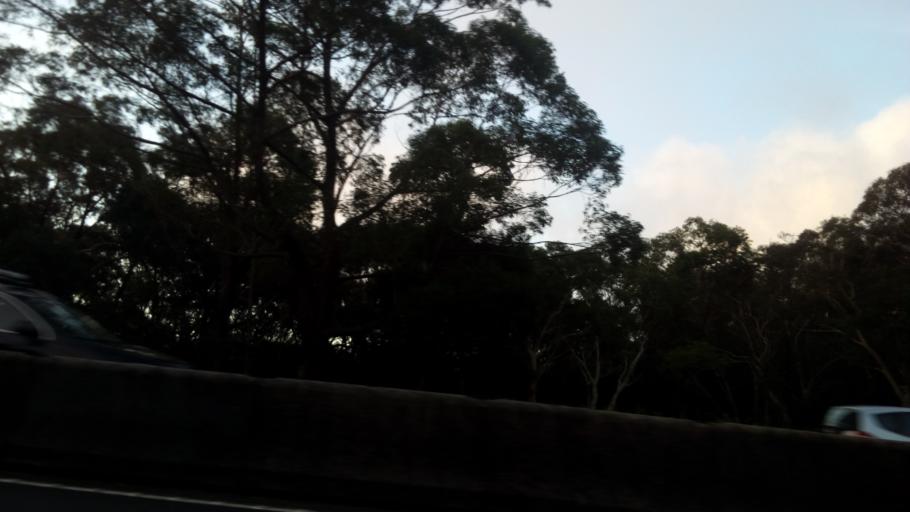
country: AU
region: New South Wales
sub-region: Wollongong
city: Mount Ousley
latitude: -34.3549
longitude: 150.8610
